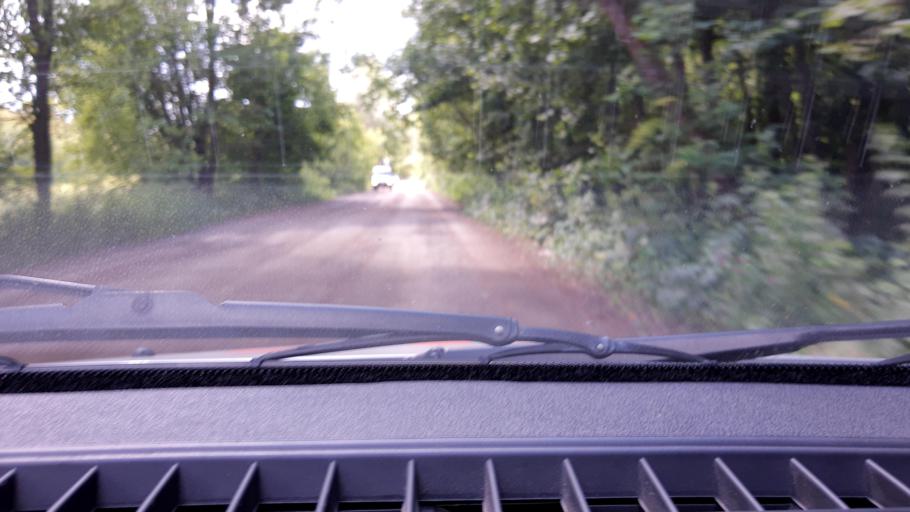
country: RU
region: Bashkortostan
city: Ufa
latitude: 54.6806
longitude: 56.0608
